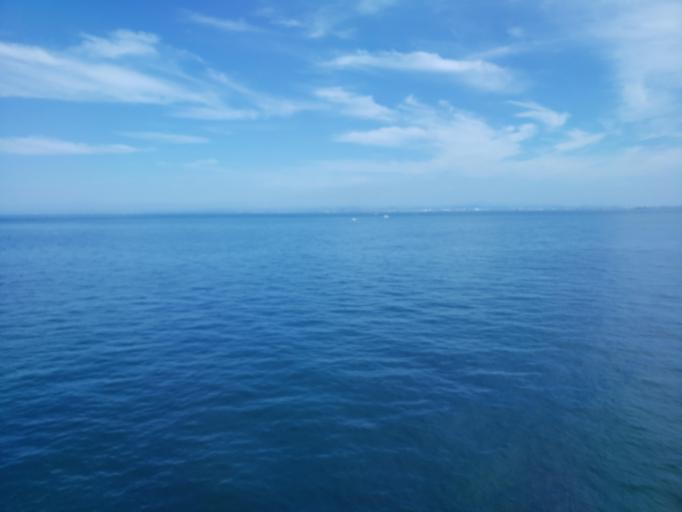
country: JP
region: Hyogo
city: Akashi
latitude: 34.5879
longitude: 134.8791
